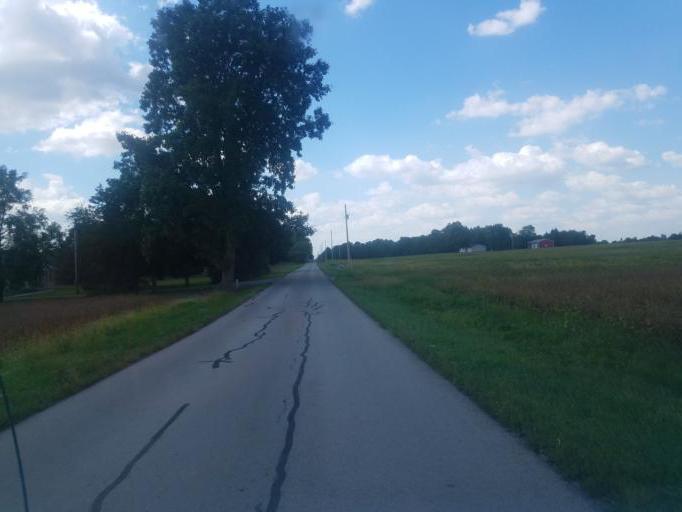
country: US
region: Ohio
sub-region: Hardin County
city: Ada
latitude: 40.6518
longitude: -83.9415
